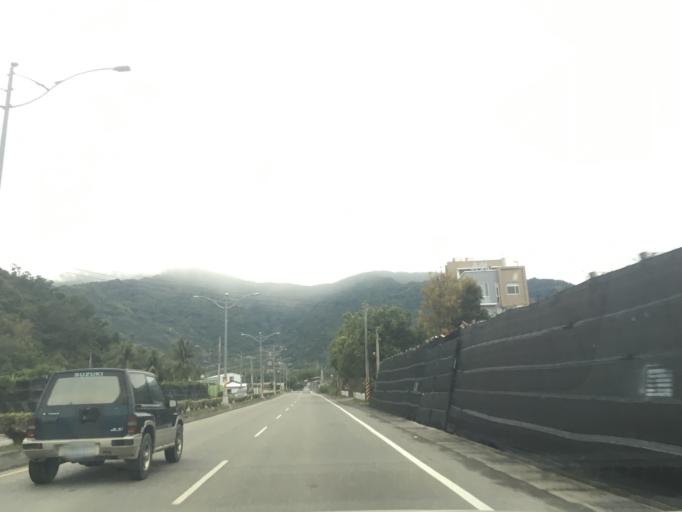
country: TW
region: Taiwan
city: Taitung City
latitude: 22.6970
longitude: 121.0436
